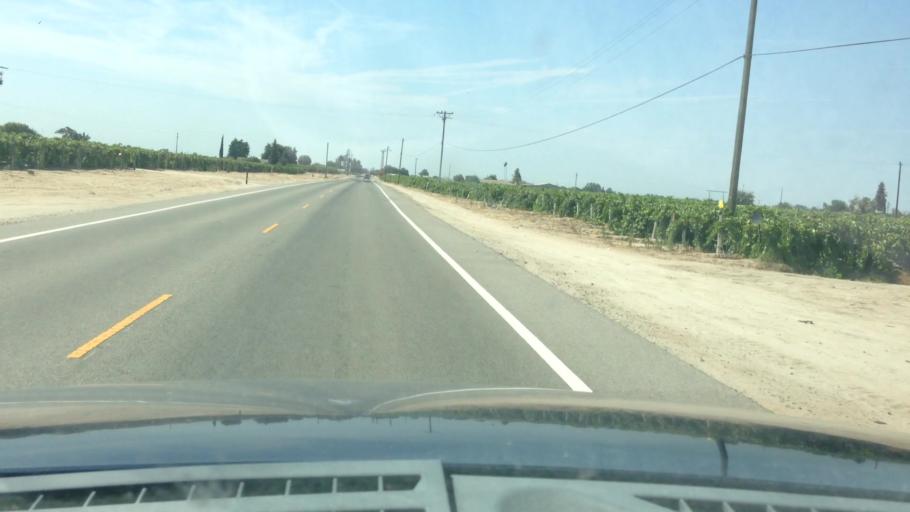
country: US
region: California
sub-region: Fresno County
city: Kingsburg
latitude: 36.5654
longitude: -119.5567
